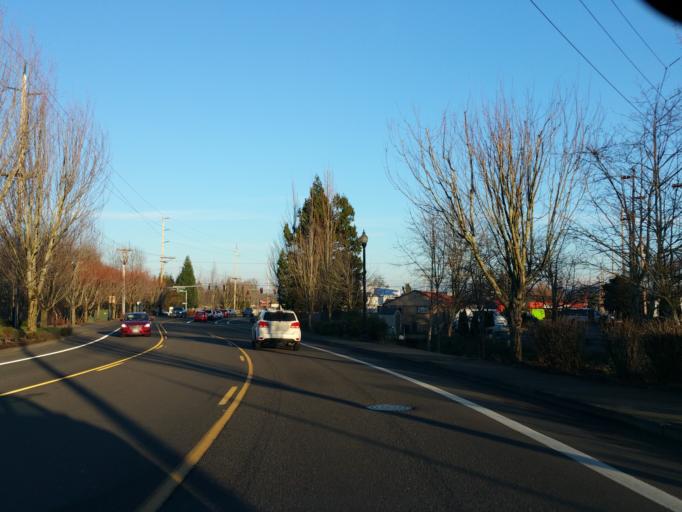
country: US
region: Oregon
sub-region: Multnomah County
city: Fairview
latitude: 45.5345
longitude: -122.4357
